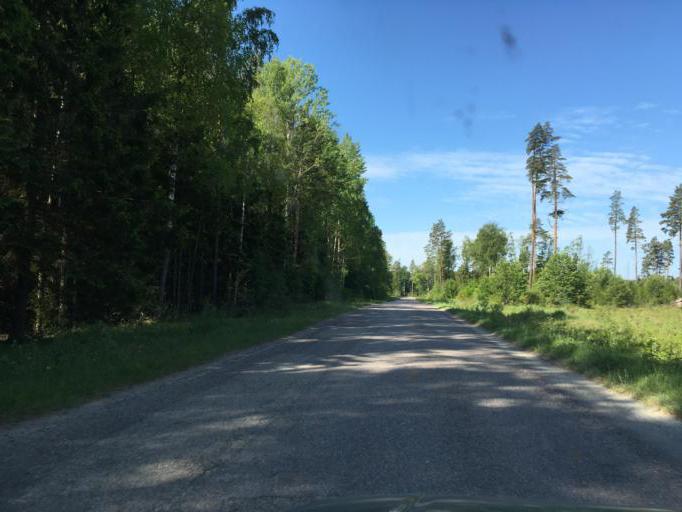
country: LV
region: Ventspils
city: Ventspils
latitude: 57.4921
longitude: 21.7974
